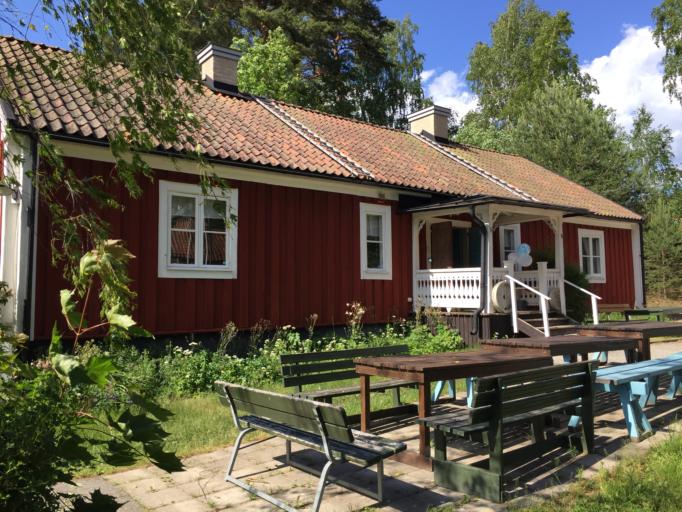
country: SE
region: Stockholm
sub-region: Botkyrka Kommun
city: Varsta
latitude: 59.1623
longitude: 17.7983
